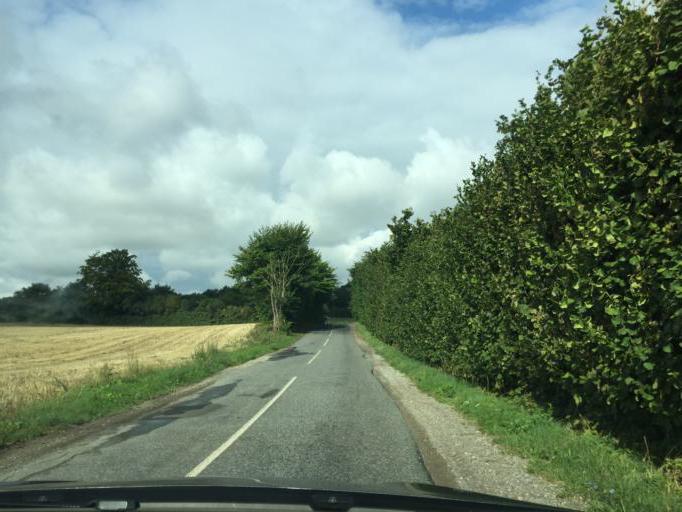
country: DK
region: South Denmark
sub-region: Assens Kommune
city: Harby
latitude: 55.1982
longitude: 10.1860
